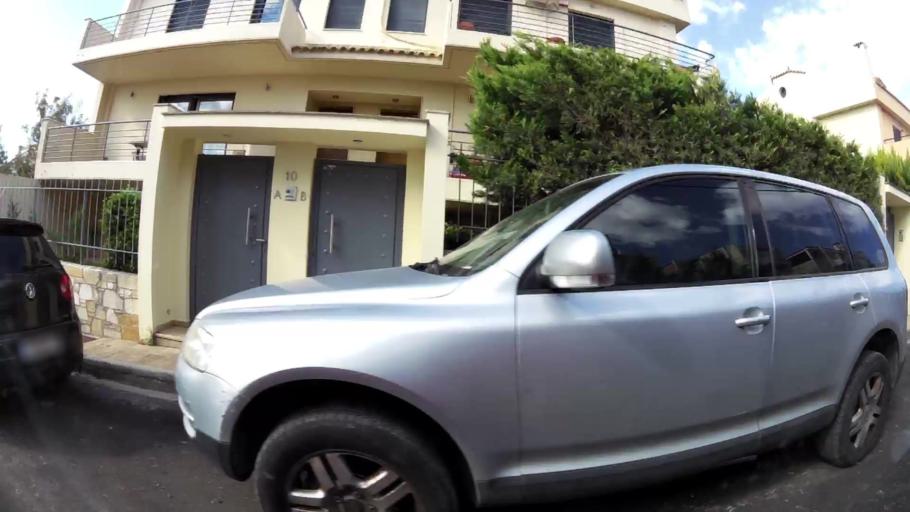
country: GR
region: Attica
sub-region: Nomarchia Anatolikis Attikis
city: Thrakomakedones
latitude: 38.1205
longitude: 23.7521
